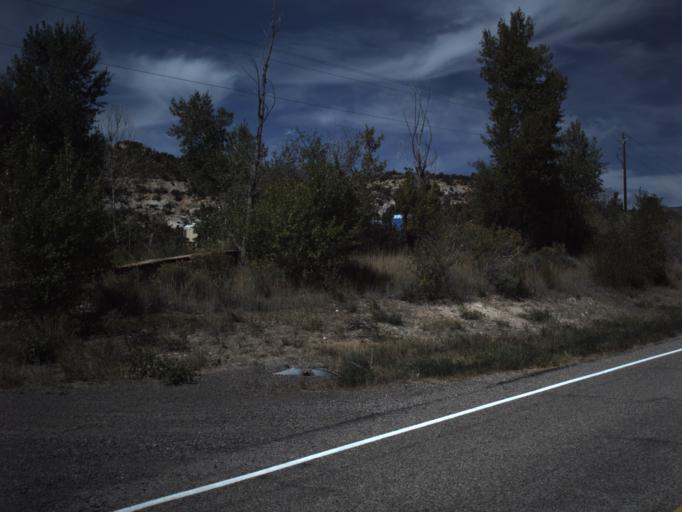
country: US
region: Utah
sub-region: Wayne County
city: Loa
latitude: 37.9142
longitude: -111.4243
